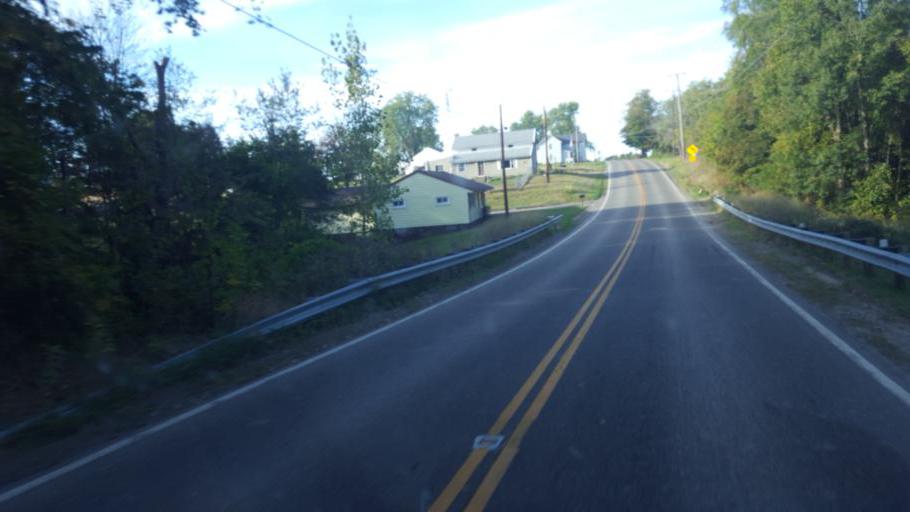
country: US
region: Ohio
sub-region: Ashland County
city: Ashland
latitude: 40.8644
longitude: -82.4029
